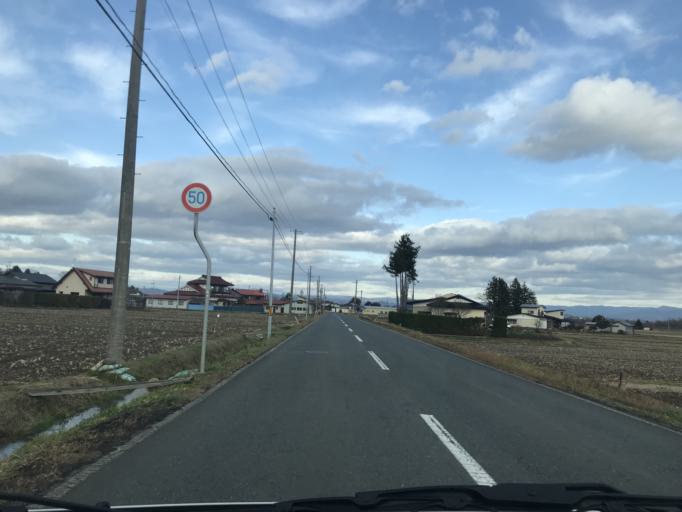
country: JP
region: Iwate
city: Mizusawa
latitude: 39.1711
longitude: 141.0896
